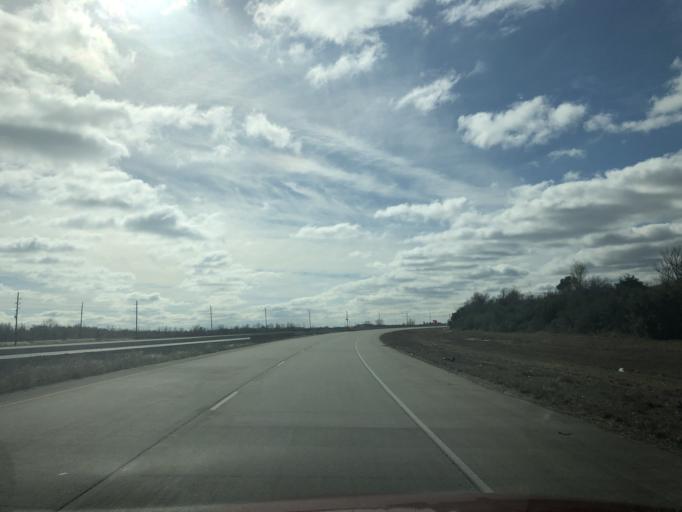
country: US
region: Texas
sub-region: Chambers County
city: Mont Belvieu
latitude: 29.8147
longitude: -94.8623
